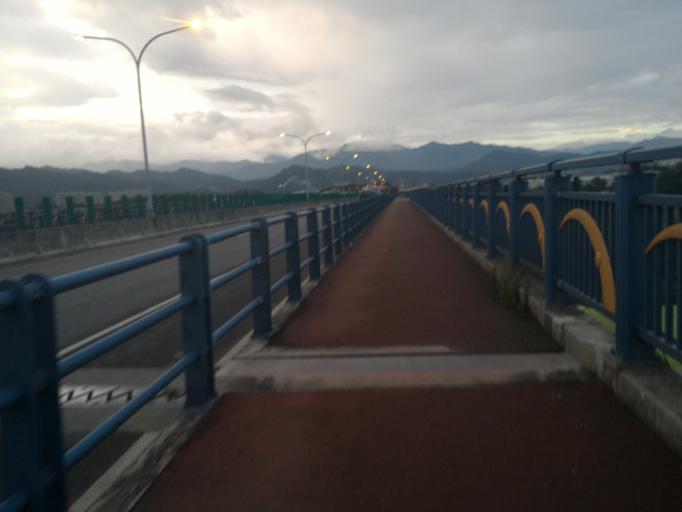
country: TW
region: Taipei
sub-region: Taipei
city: Banqiao
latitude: 24.9677
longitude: 121.4046
